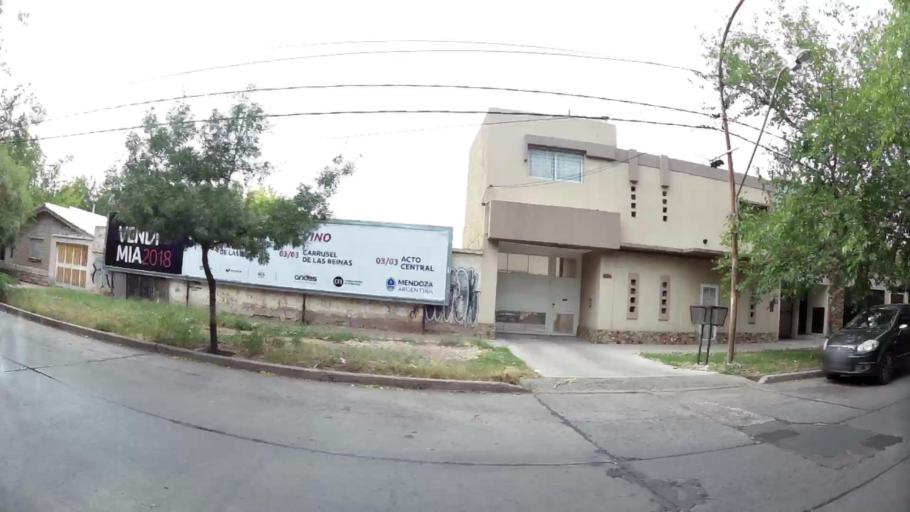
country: AR
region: Mendoza
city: Mendoza
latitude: -32.8743
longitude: -68.8557
